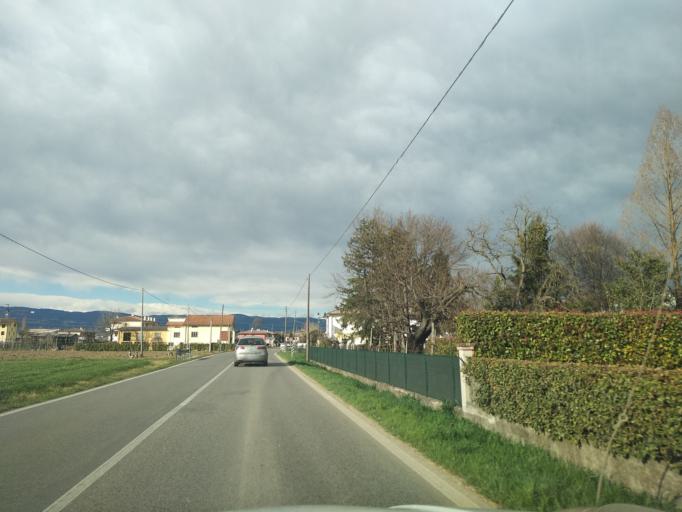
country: IT
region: Veneto
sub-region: Provincia di Vicenza
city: Poianella
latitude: 45.6267
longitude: 11.6231
